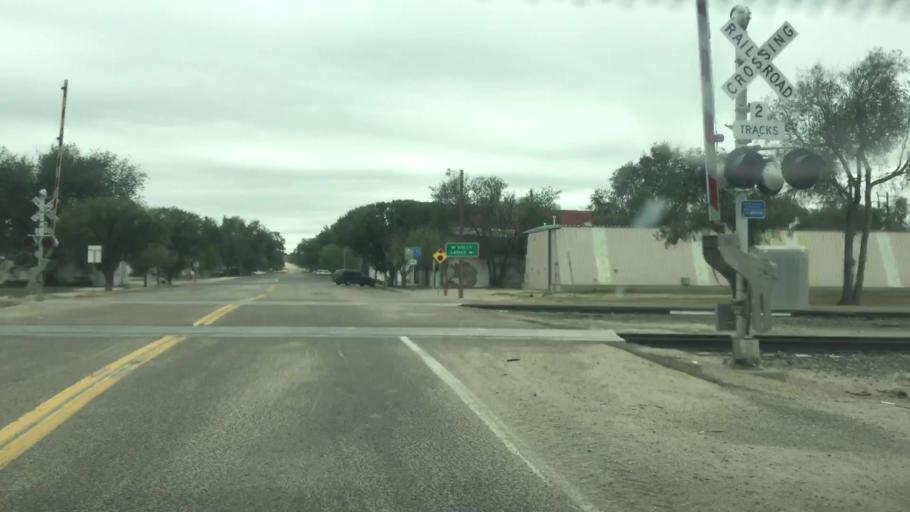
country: US
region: Colorado
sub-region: Prowers County
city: Lamar
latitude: 38.0638
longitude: -102.3104
